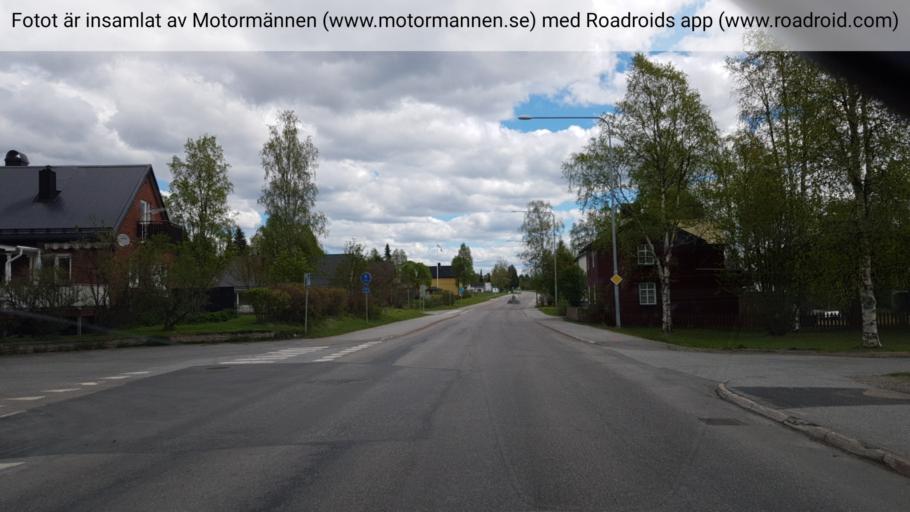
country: SE
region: Vaesterbotten
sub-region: Norsjo Kommun
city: Norsjoe
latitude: 64.9101
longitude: 19.4914
